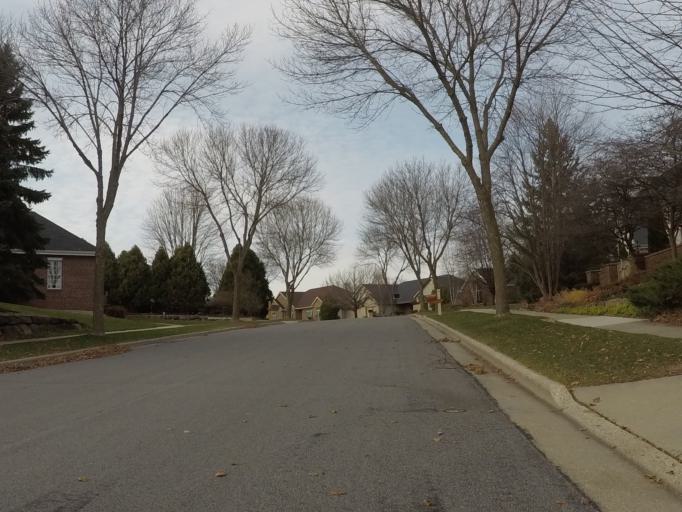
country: US
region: Wisconsin
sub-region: Dane County
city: Middleton
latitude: 43.0803
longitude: -89.5434
